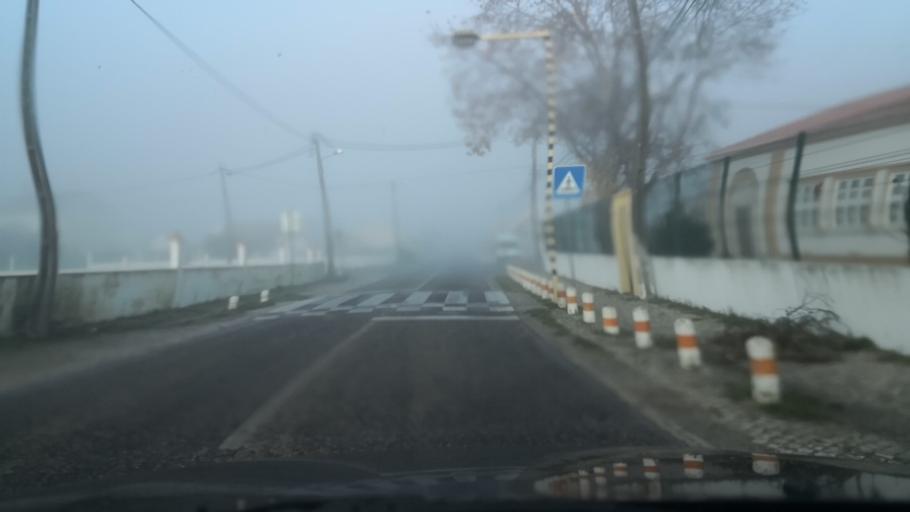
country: PT
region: Setubal
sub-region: Palmela
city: Pinhal Novo
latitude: 38.6129
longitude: -8.8799
